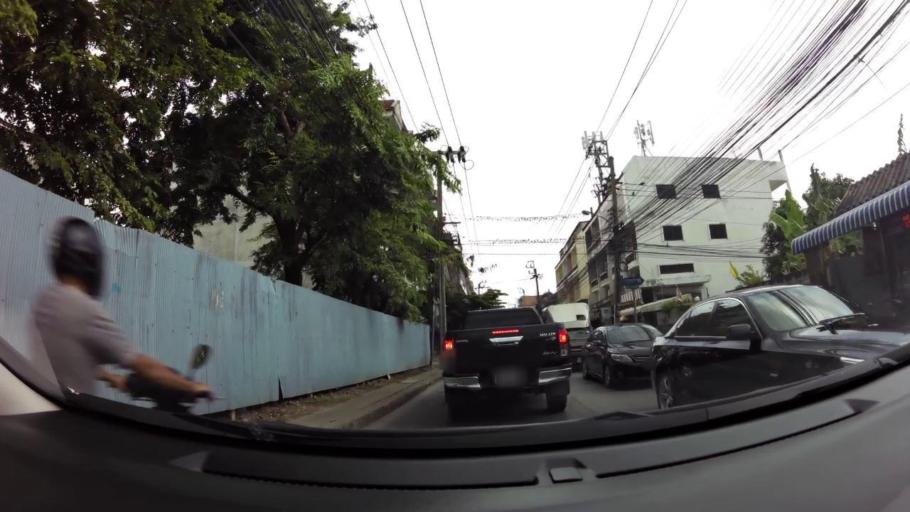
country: TH
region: Bangkok
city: Bang Na
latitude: 13.6850
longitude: 100.6355
